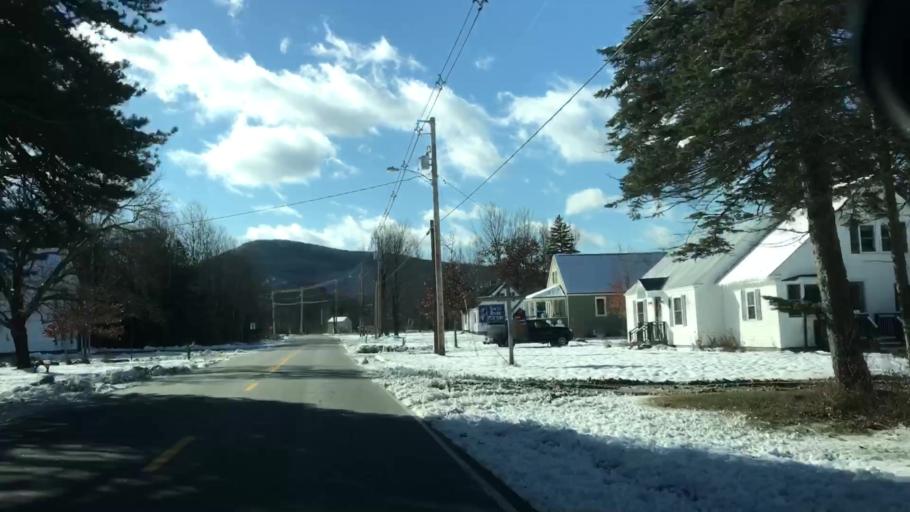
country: US
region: Maine
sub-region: Oxford County
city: Brownfield
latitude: 43.9492
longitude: -70.8866
